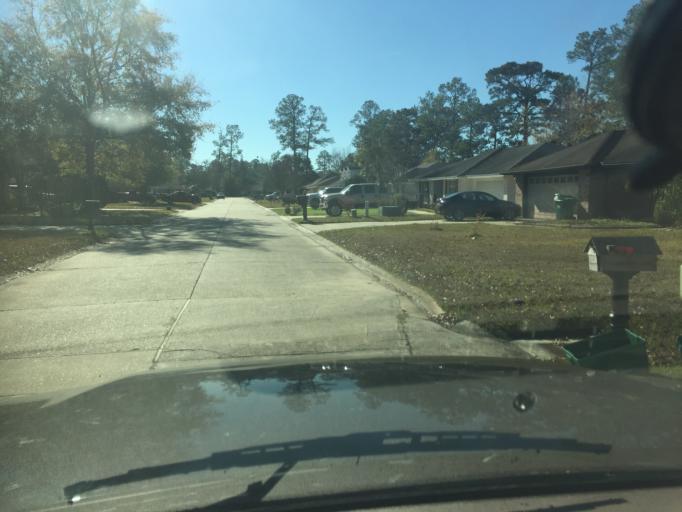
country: US
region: Louisiana
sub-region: Saint Tammany Parish
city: Slidell
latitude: 30.3030
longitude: -89.7373
